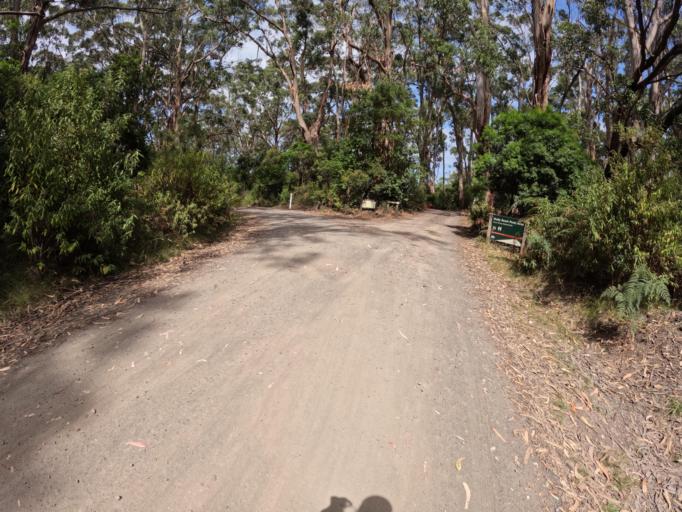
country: AU
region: Victoria
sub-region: Colac-Otway
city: Apollo Bay
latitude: -38.7899
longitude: 143.6192
